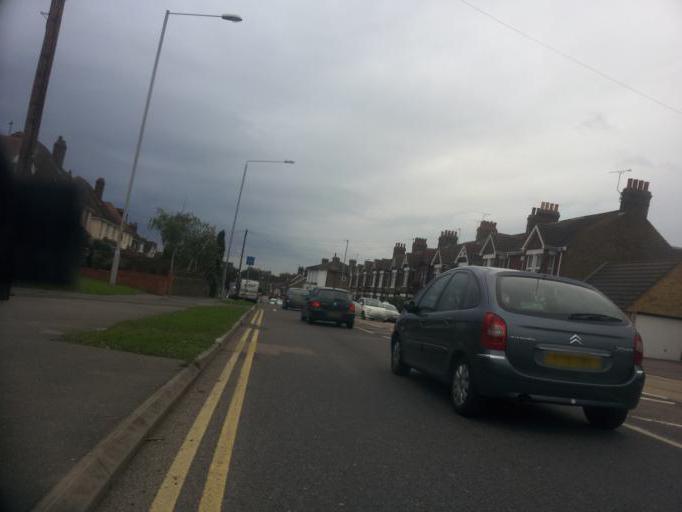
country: GB
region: England
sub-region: Kent
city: Sittingbourne
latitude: 51.3362
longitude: 0.7578
